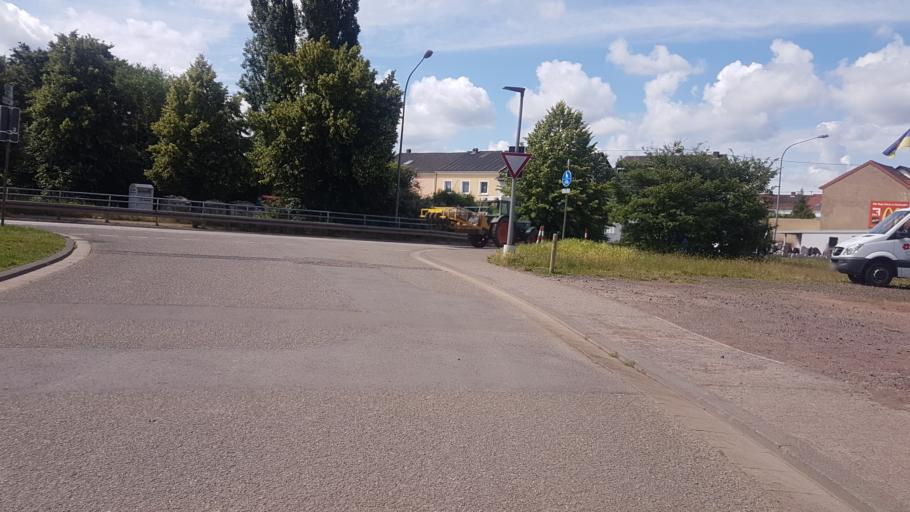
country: DE
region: Saarland
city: Saarlouis
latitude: 49.3069
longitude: 6.7608
